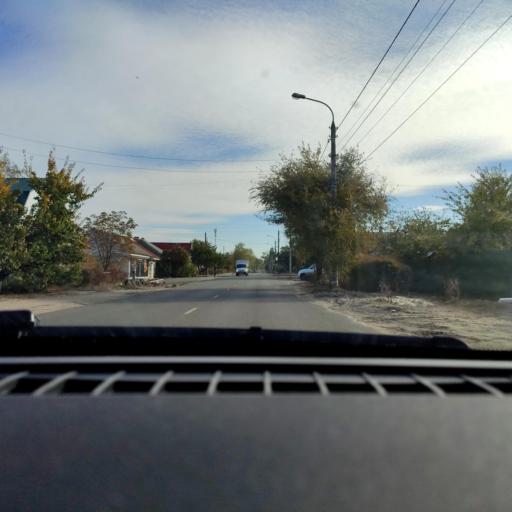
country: RU
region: Voronezj
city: Maslovka
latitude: 51.6103
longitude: 39.2238
